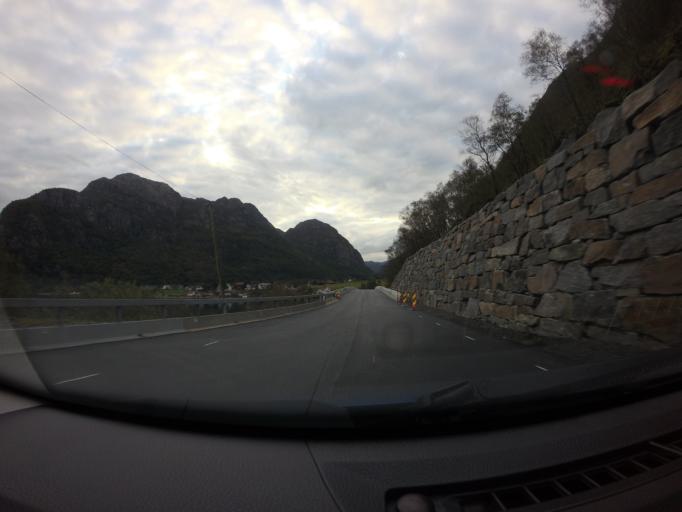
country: NO
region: Rogaland
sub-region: Forsand
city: Forsand
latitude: 58.8361
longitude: 6.1724
